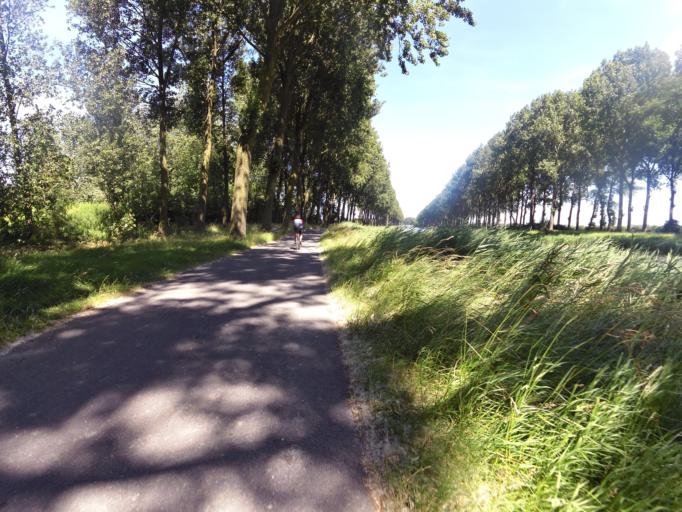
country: NL
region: Zeeland
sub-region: Gemeente Sluis
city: Sluis
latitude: 51.3029
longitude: 3.3600
